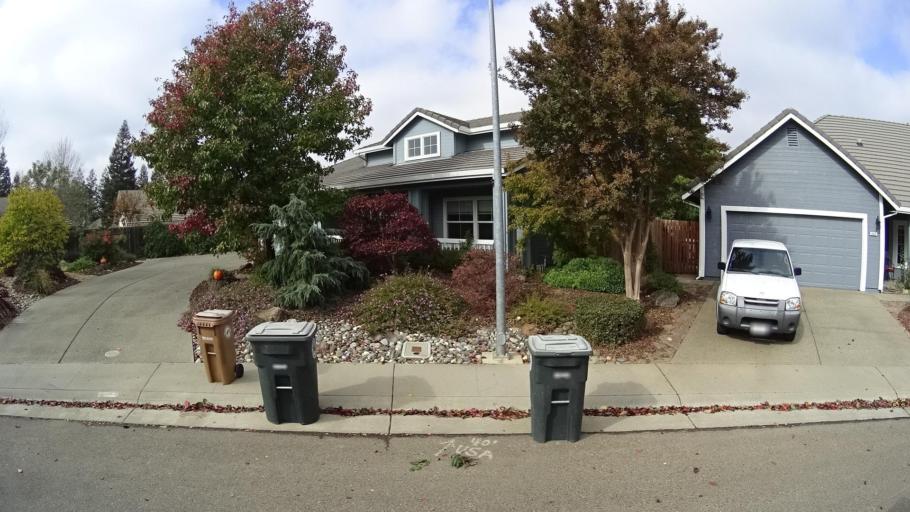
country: US
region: California
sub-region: Sacramento County
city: Elk Grove
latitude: 38.4248
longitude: -121.3642
